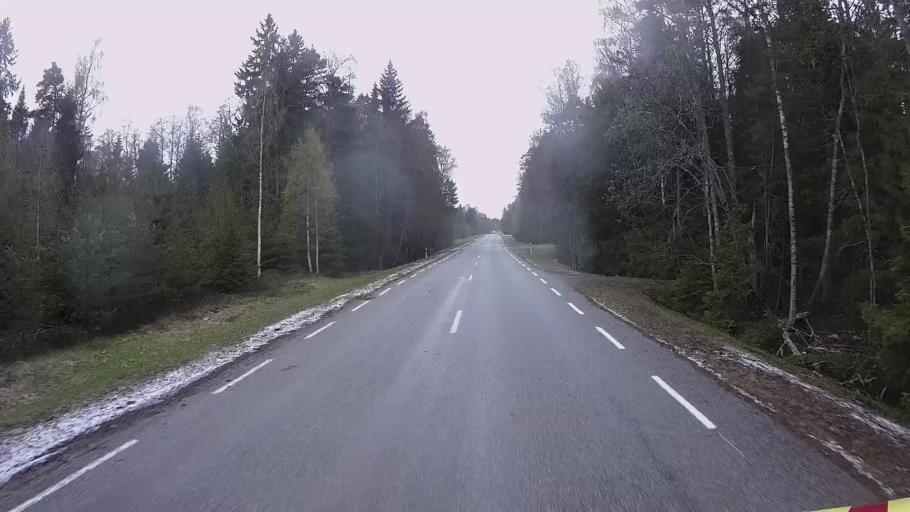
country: EE
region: Hiiumaa
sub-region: Kaerdla linn
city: Kardla
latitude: 59.0644
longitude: 22.6863
